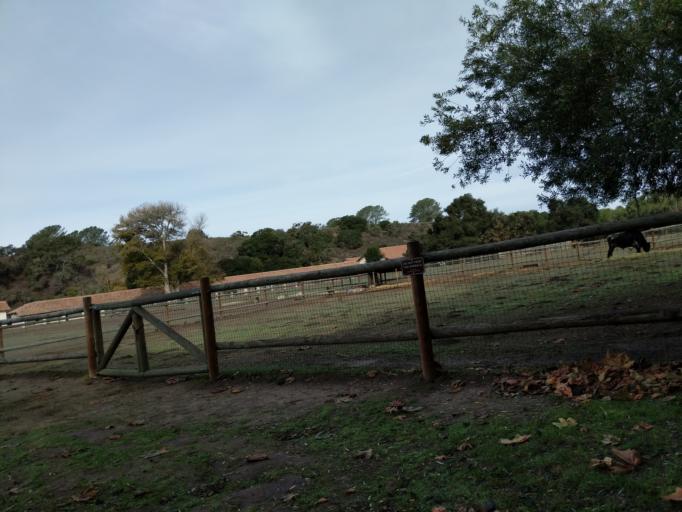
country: US
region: California
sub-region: Santa Barbara County
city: Mission Hills
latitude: 34.6707
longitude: -120.4209
